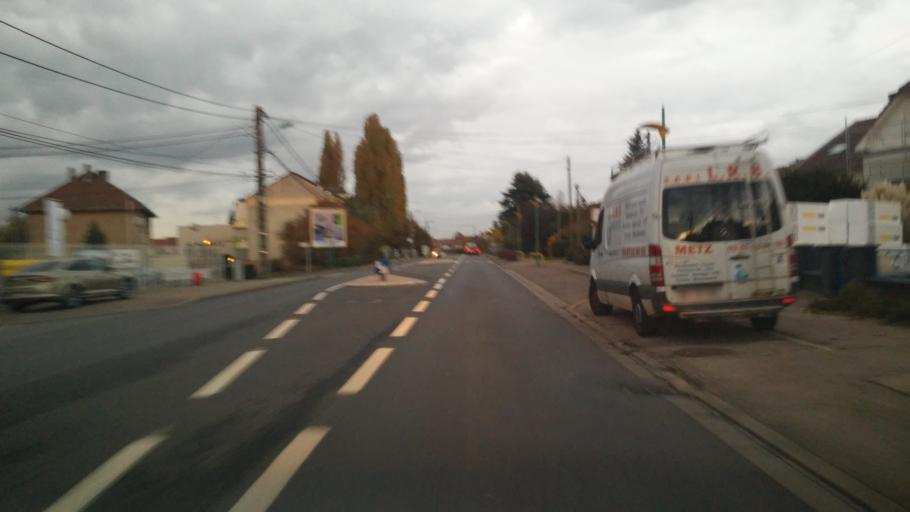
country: FR
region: Lorraine
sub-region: Departement de la Moselle
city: Maizieres-les-Metz
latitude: 49.2217
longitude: 6.1642
